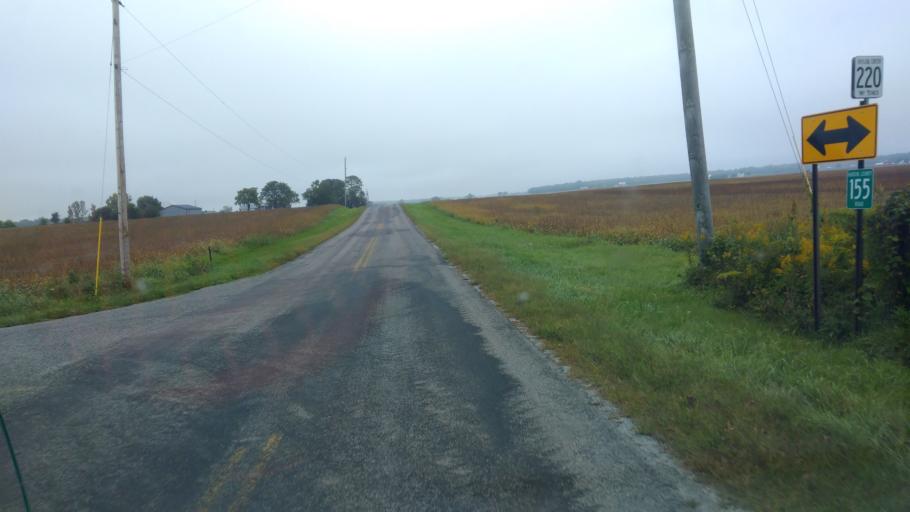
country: US
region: Ohio
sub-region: Hardin County
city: Kenton
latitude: 40.5328
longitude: -83.6303
